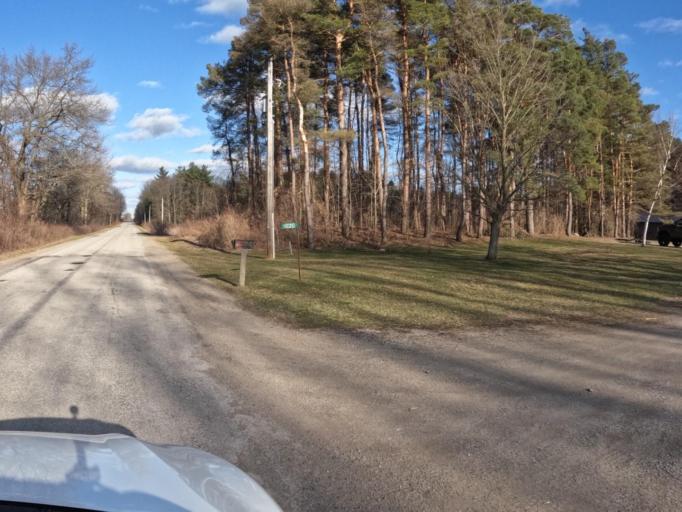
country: CA
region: Ontario
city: Norfolk County
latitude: 42.8153
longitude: -80.5561
